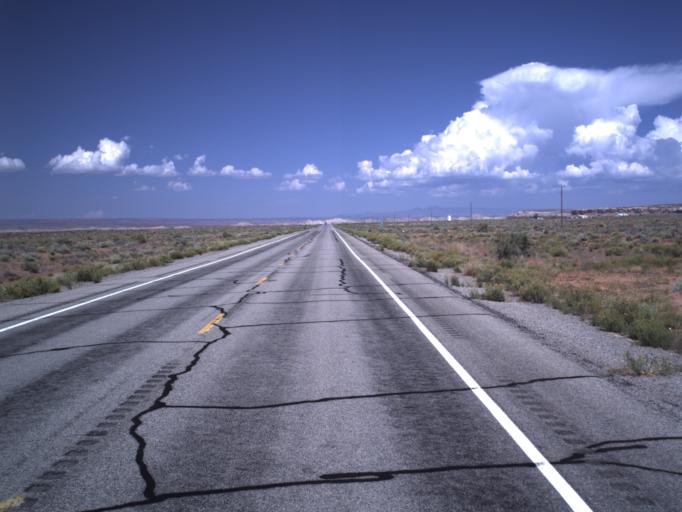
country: US
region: Utah
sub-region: San Juan County
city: Blanding
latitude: 37.1735
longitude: -109.5823
